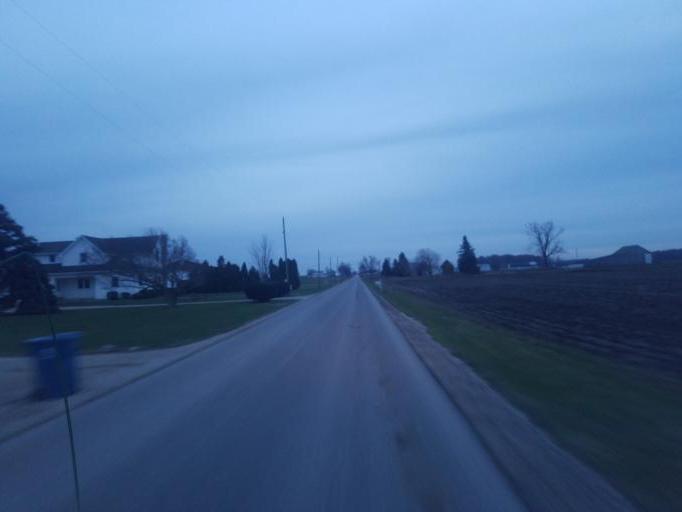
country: US
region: Indiana
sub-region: Adams County
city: Berne
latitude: 40.7191
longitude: -84.8984
